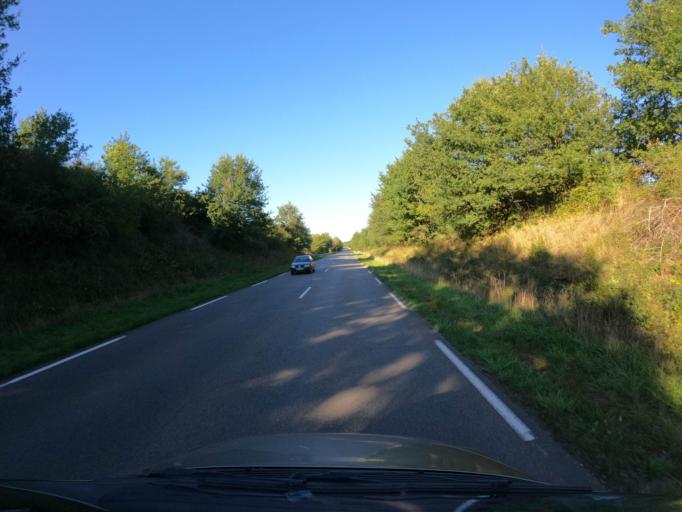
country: FR
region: Bourgogne
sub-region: Departement de Saone-et-Loire
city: Saint-Eusebe
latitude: 46.7164
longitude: 4.4260
